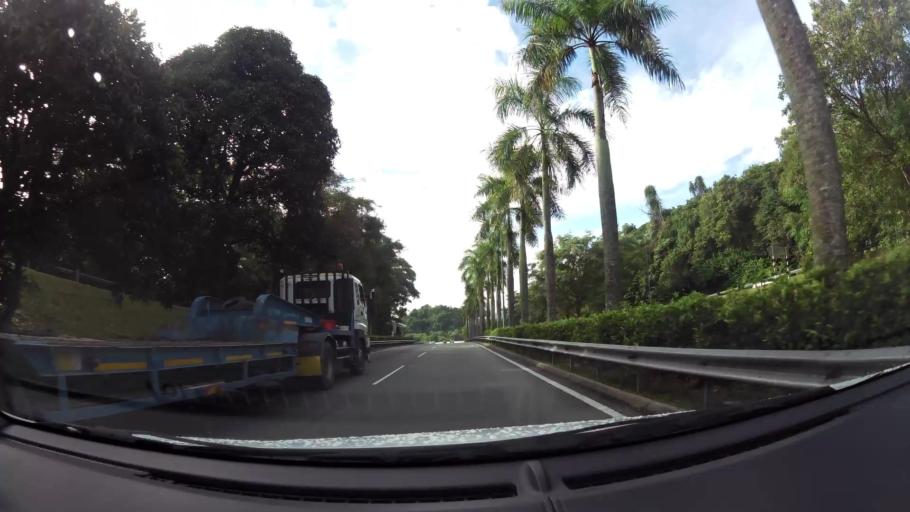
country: BN
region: Brunei and Muara
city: Bandar Seri Begawan
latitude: 4.8917
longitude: 114.9300
